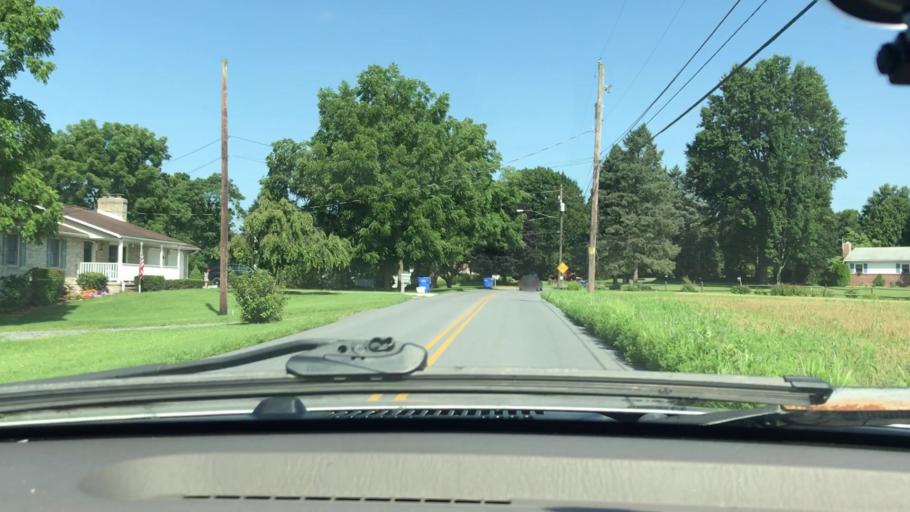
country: US
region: Pennsylvania
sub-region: Dauphin County
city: Rutherford
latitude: 40.2548
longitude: -76.7457
